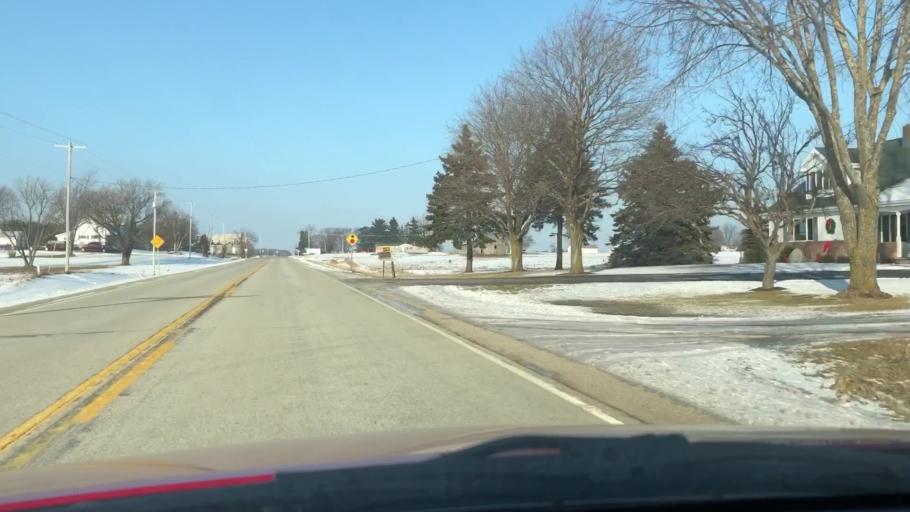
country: US
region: Wisconsin
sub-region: Outagamie County
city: Black Creek
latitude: 44.4114
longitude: -88.3744
